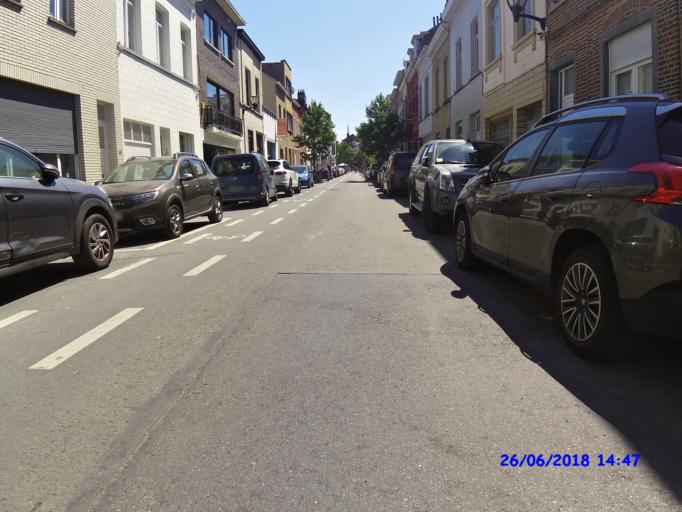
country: BE
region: Brussels Capital
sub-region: Bruxelles-Capitale
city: Brussels
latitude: 50.8745
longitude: 4.3253
